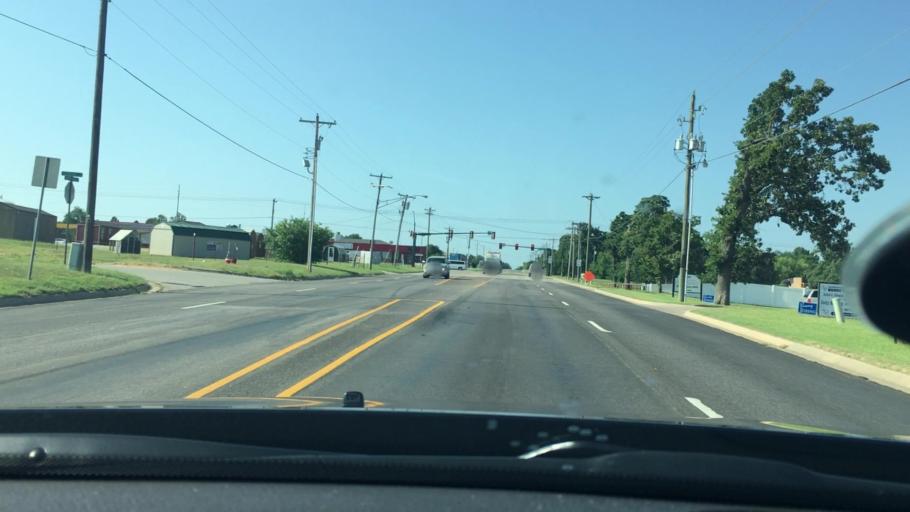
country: US
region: Oklahoma
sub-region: Pontotoc County
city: Ada
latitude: 34.7831
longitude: -96.6349
